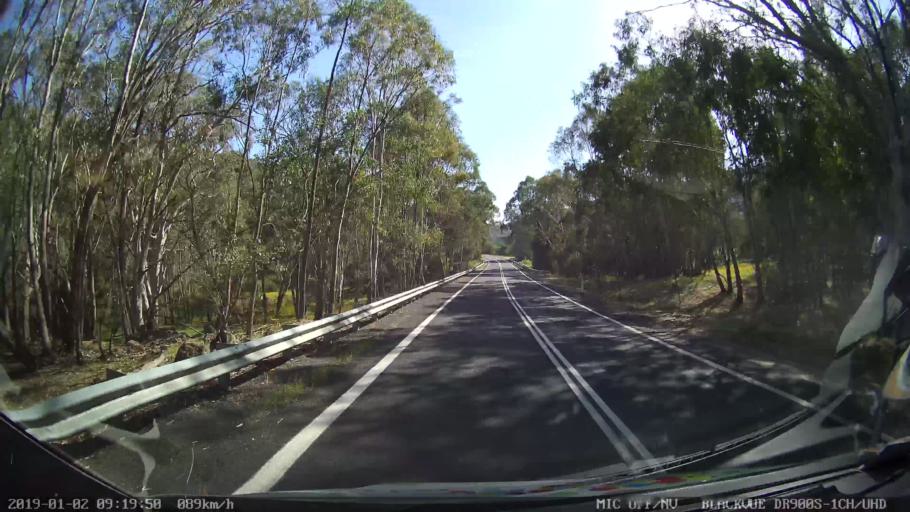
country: AU
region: New South Wales
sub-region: Tumut Shire
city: Tumut
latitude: -35.4178
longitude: 148.2778
